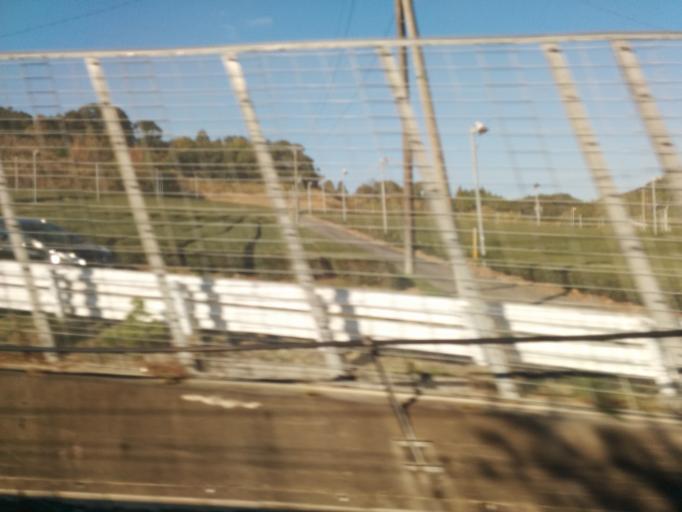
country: JP
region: Shizuoka
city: Kakegawa
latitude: 34.7720
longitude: 138.0799
